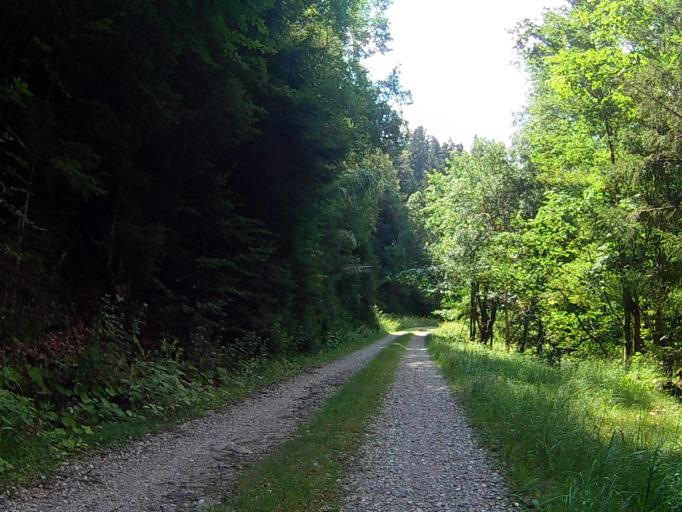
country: SI
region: Selnica ob Dravi
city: Selnica ob Dravi
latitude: 46.4938
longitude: 15.4633
